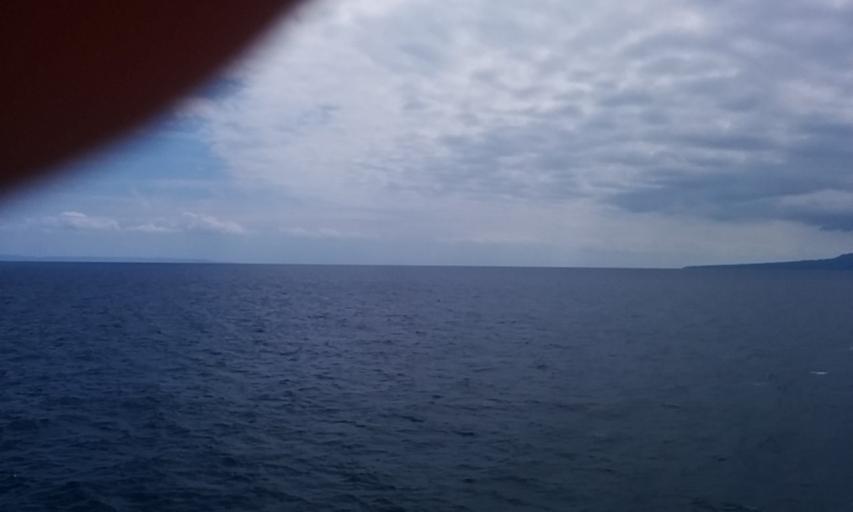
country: JP
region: Kagoshima
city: Nishinoomote
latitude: 30.5155
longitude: 130.6119
